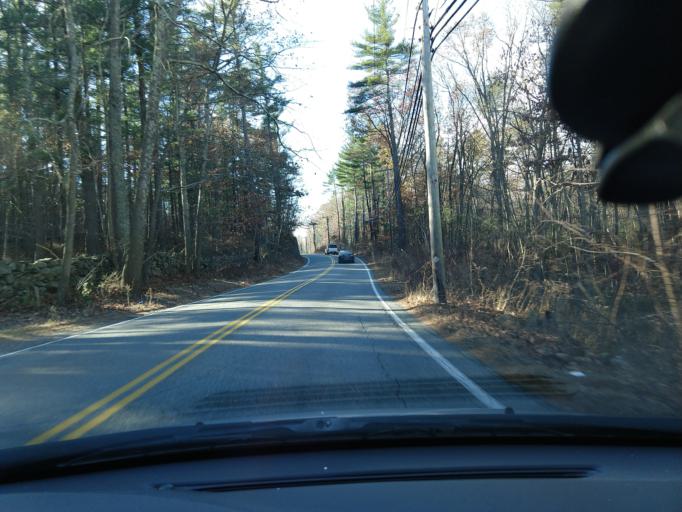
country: US
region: Massachusetts
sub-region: Middlesex County
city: Dunstable
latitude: 42.6810
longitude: -71.4626
